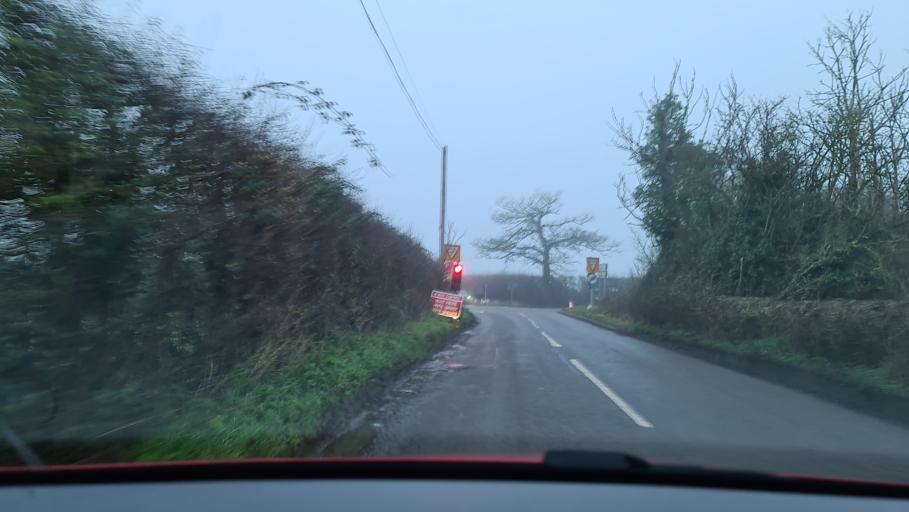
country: GB
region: England
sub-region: Buckinghamshire
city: Waddesdon
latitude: 51.8642
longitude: -0.8902
